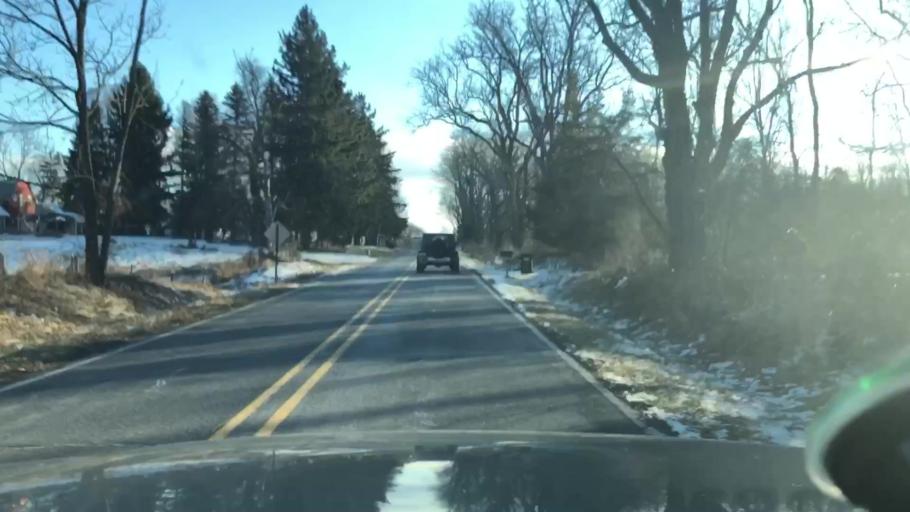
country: US
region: Michigan
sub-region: Jackson County
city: Vandercook Lake
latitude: 42.1224
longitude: -84.4515
